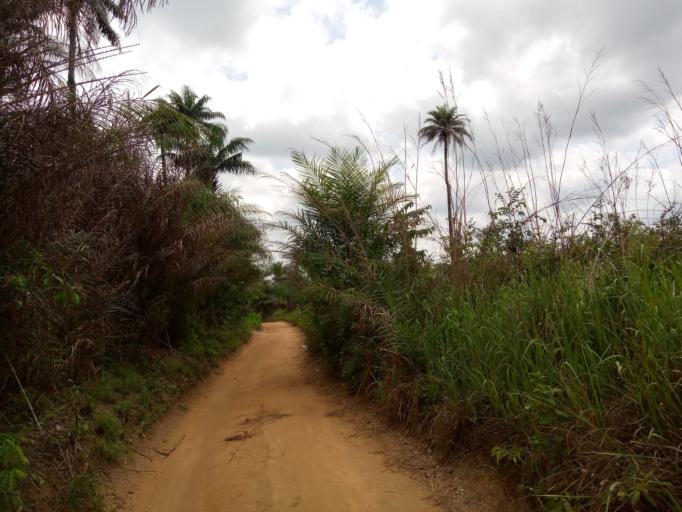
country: SL
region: Western Area
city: Waterloo
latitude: 8.3947
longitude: -12.9464
